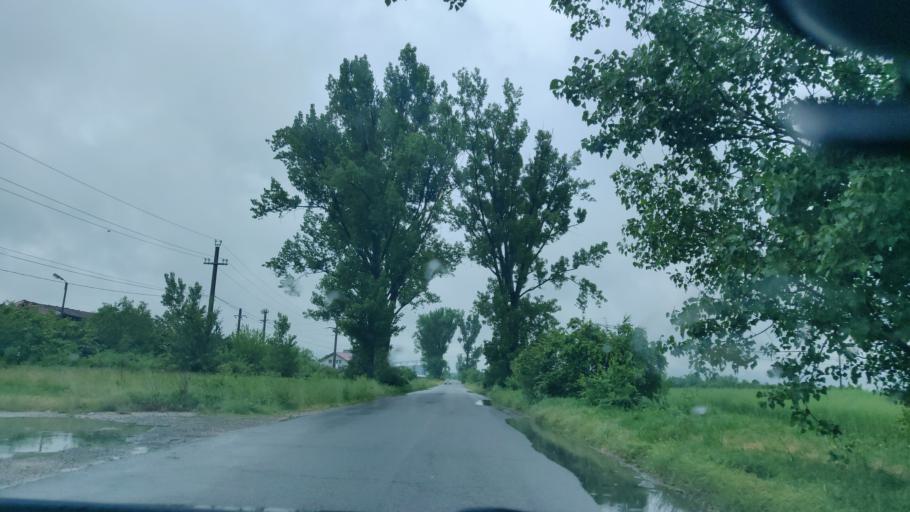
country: RO
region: Giurgiu
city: Iepuresti
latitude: 44.2690
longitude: 25.8466
